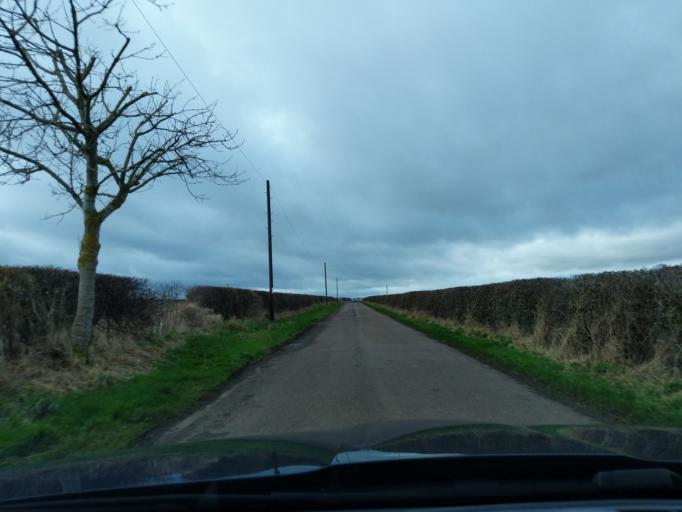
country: GB
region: England
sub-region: Northumberland
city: Ancroft
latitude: 55.6960
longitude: -1.9955
